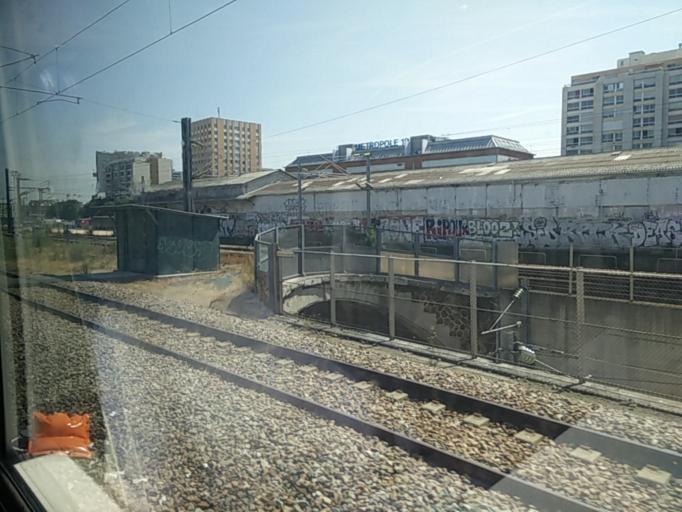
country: FR
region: Ile-de-France
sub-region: Departement de Seine-Saint-Denis
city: Aubervilliers
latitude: 48.8917
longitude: 2.3675
